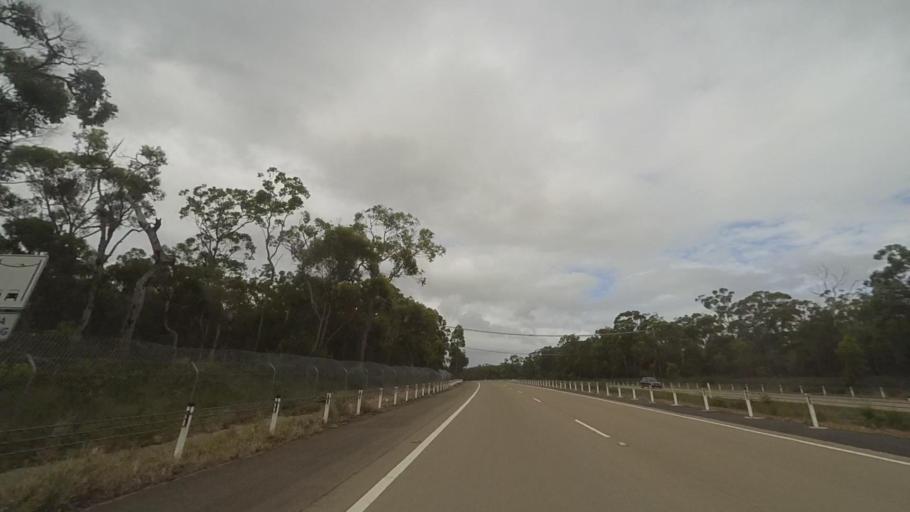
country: AU
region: New South Wales
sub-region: Port Stephens Shire
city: Medowie
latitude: -32.6448
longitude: 151.9254
